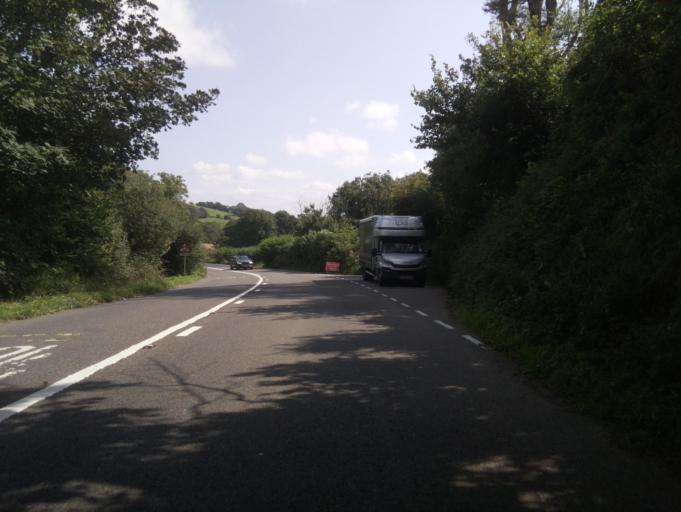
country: GB
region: England
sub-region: Devon
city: Ivybridge
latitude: 50.3523
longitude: -3.9319
